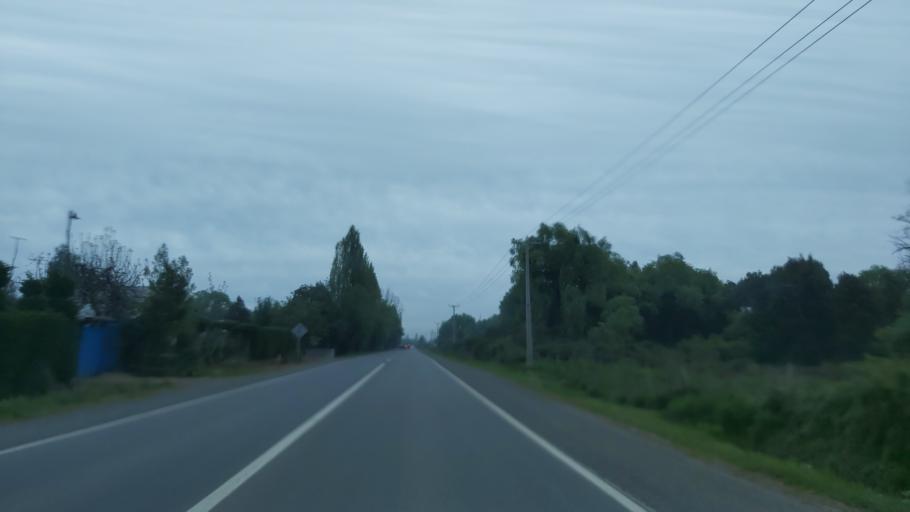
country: CL
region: Maule
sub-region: Provincia de Linares
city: Linares
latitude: -35.7622
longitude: -71.5089
